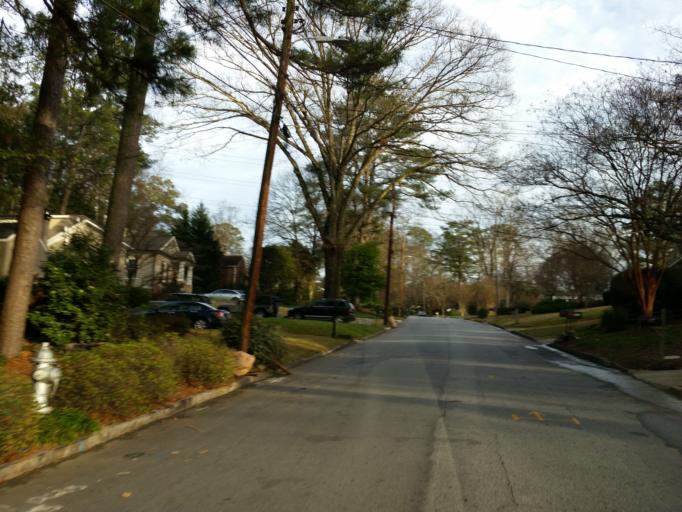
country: US
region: Georgia
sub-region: DeKalb County
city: Druid Hills
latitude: 33.7930
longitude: -84.3665
